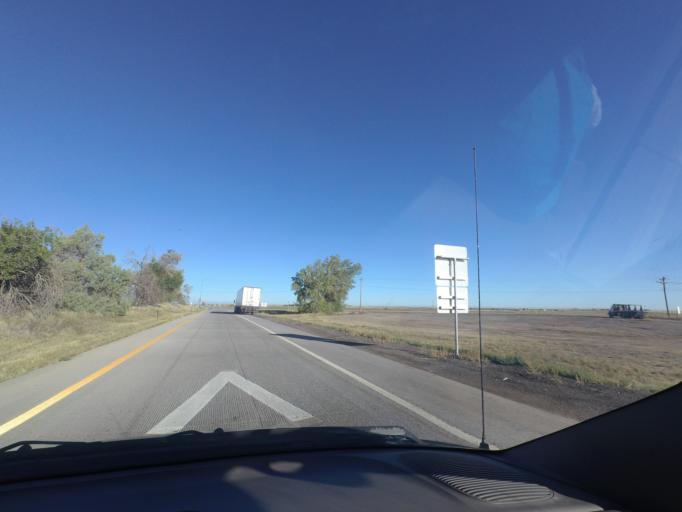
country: US
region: Colorado
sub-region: Adams County
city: Bennett
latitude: 39.7371
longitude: -104.3964
